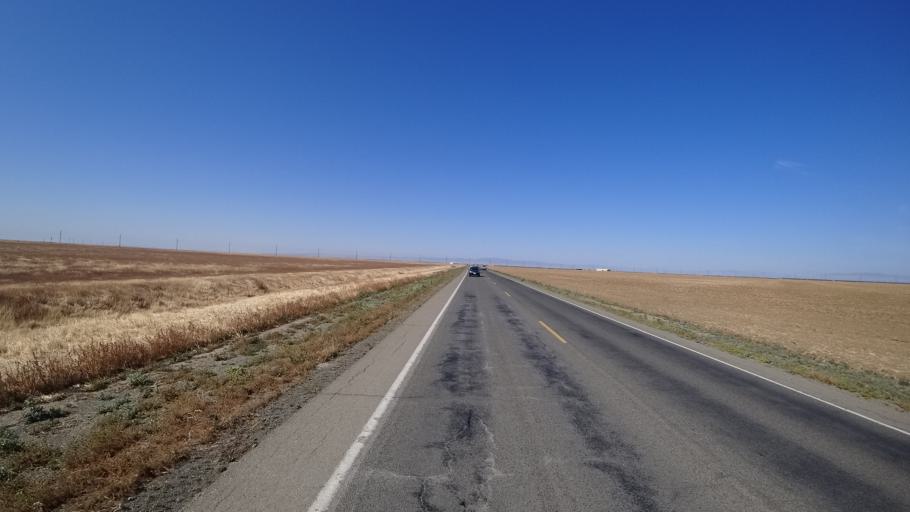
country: US
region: California
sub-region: Kings County
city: Lemoore Station
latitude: 36.2333
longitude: -119.8892
